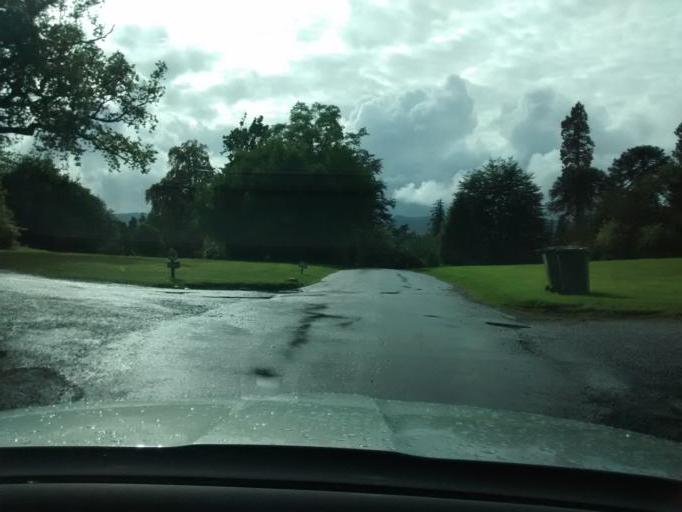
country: GB
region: Scotland
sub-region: North Ayrshire
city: Isle of Arran
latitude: 55.5947
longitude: -5.1512
